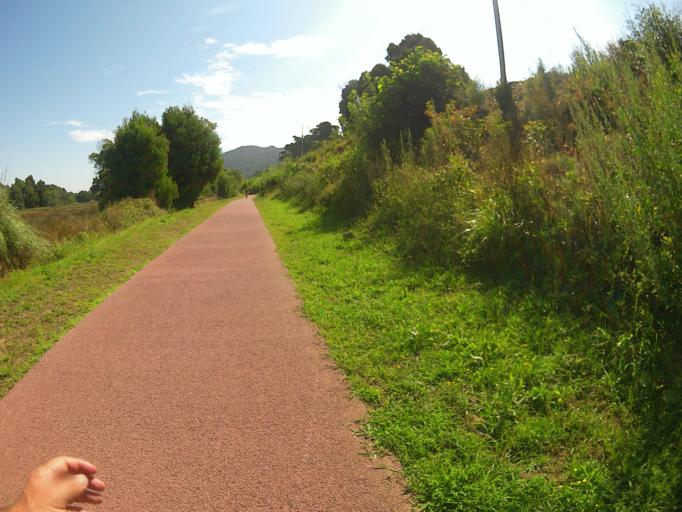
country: ES
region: Galicia
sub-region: Provincia de Pontevedra
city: O Rosal
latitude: 41.9016
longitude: -8.8076
